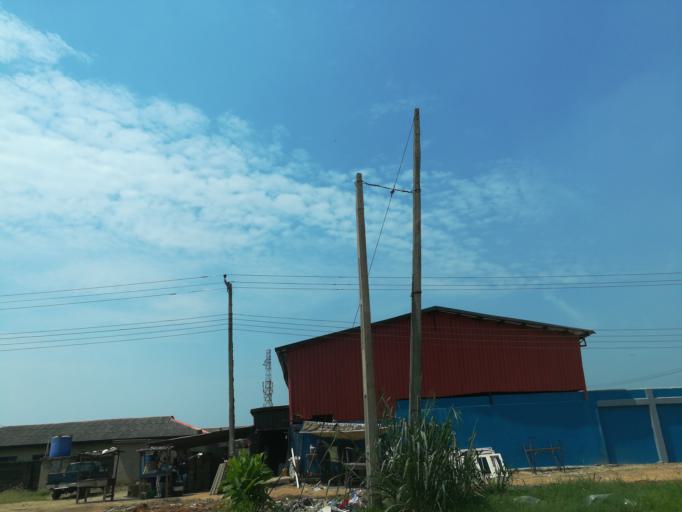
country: NG
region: Lagos
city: Ikorodu
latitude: 6.6605
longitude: 3.4717
